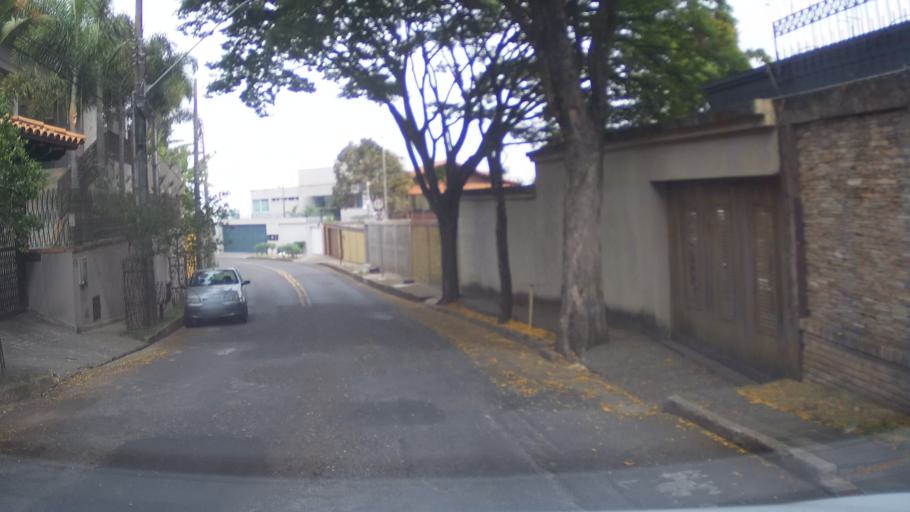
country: BR
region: Minas Gerais
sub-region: Belo Horizonte
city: Belo Horizonte
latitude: -19.9515
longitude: -43.9181
